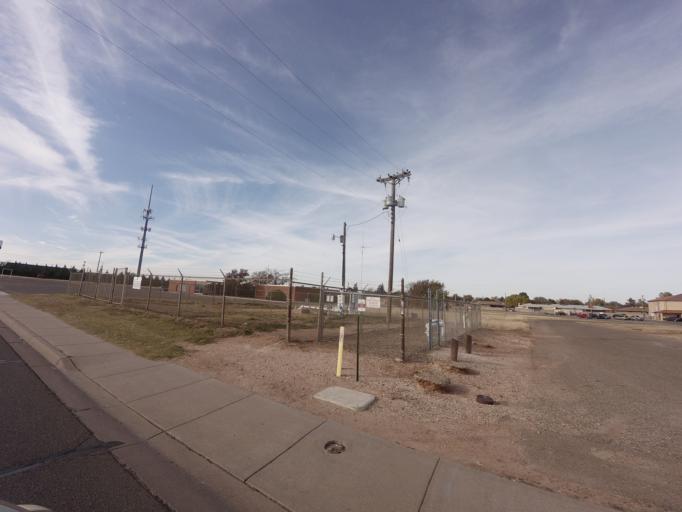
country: US
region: New Mexico
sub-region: Curry County
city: Clovis
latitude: 34.4193
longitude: -103.2155
